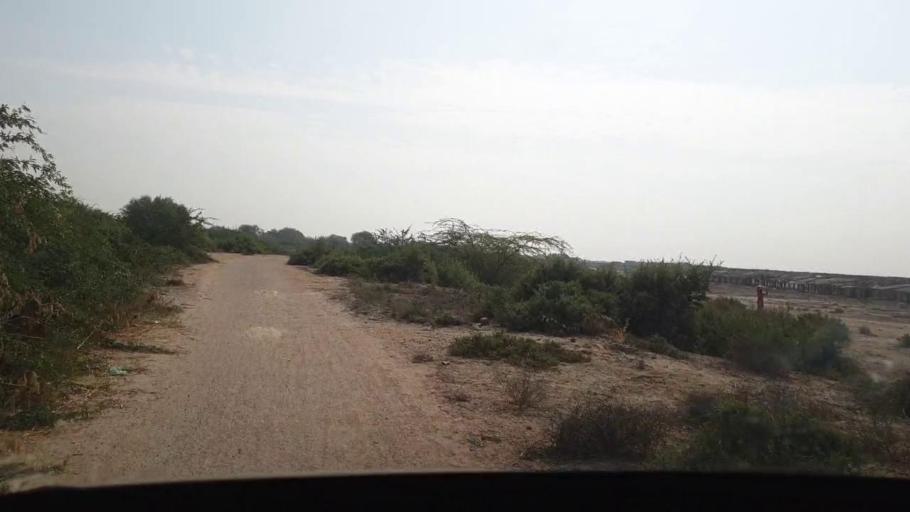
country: PK
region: Sindh
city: Chuhar Jamali
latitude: 24.2386
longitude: 67.9844
